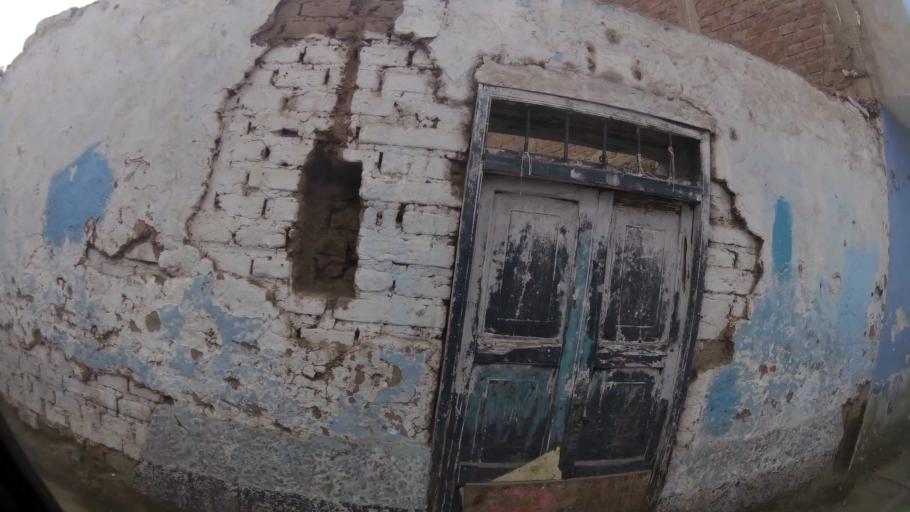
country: PE
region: Lima
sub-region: Provincia de Huaral
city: Huaral
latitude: -11.4917
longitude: -77.2083
